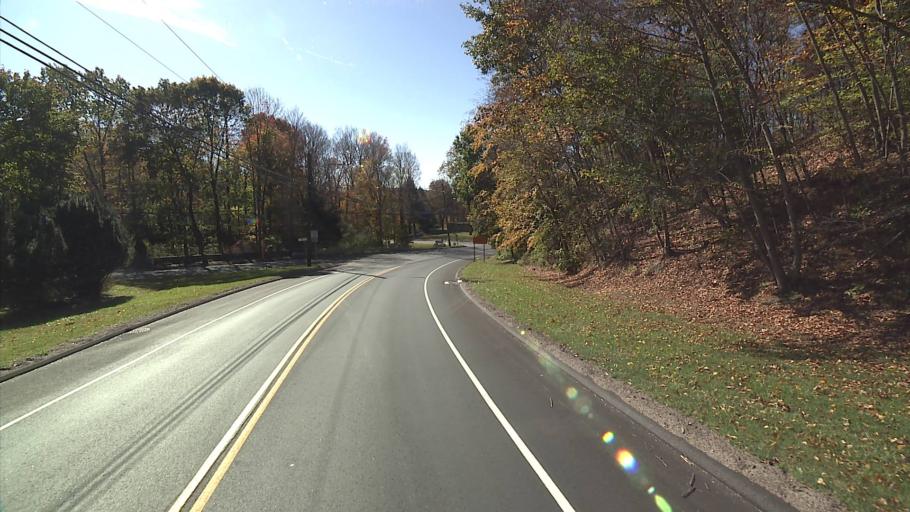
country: US
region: Connecticut
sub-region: Litchfield County
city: Watertown
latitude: 41.6130
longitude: -73.1121
